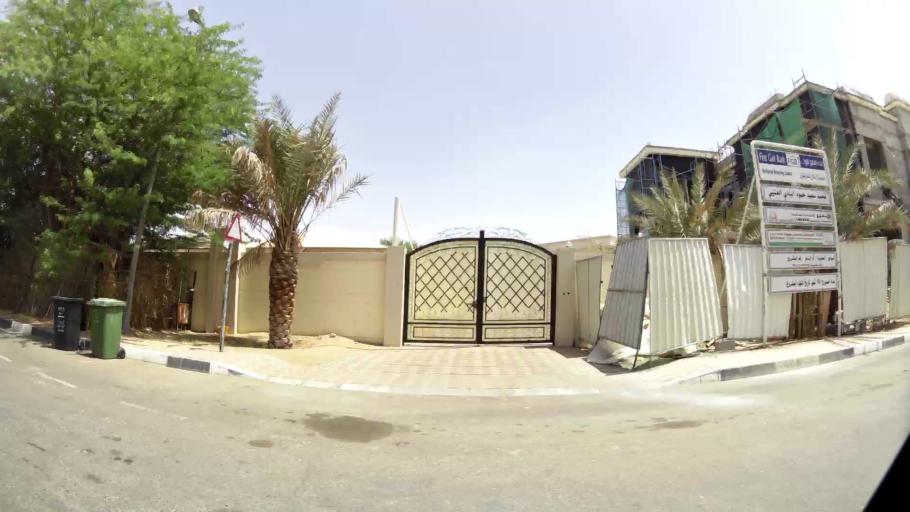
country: AE
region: Abu Dhabi
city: Al Ain
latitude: 24.2536
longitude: 55.7062
